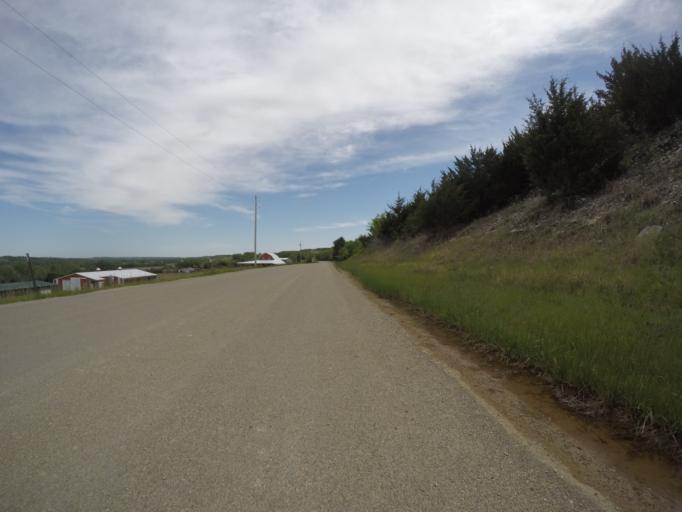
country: US
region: Kansas
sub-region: Riley County
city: Ogden
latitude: 39.0576
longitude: -96.6493
